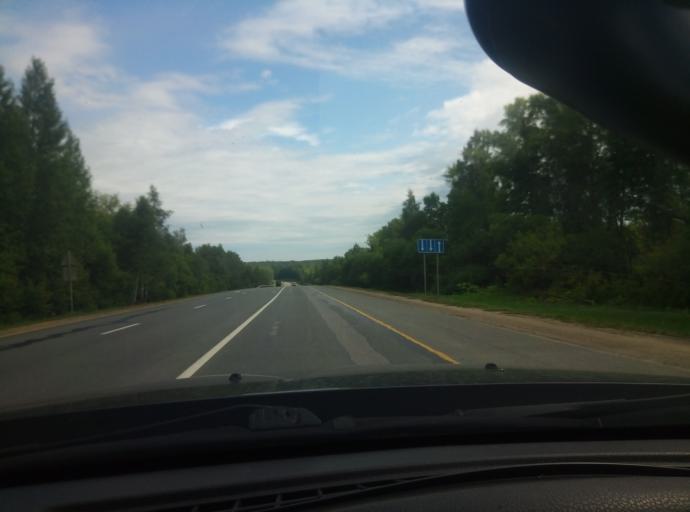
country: RU
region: Tula
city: Barsuki
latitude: 54.3113
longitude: 37.5420
